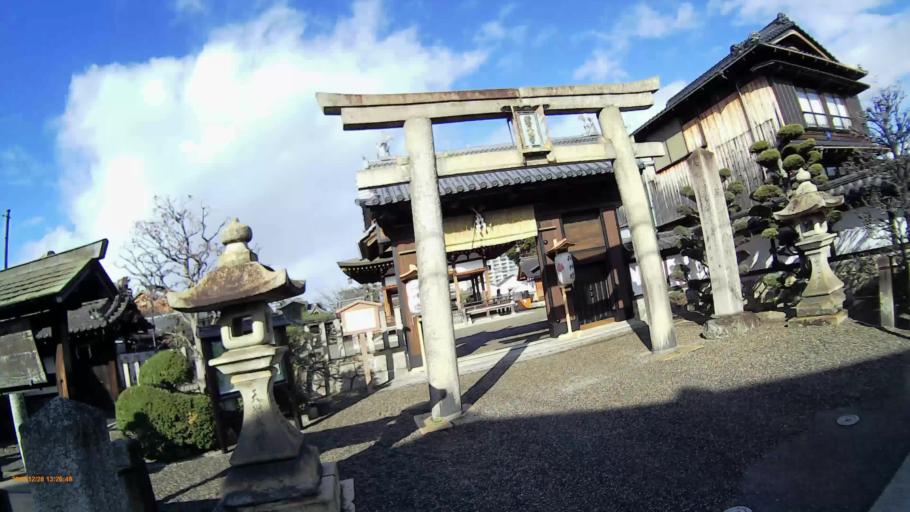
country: JP
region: Shiga Prefecture
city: Otsu-shi
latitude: 34.9874
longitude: 135.8948
